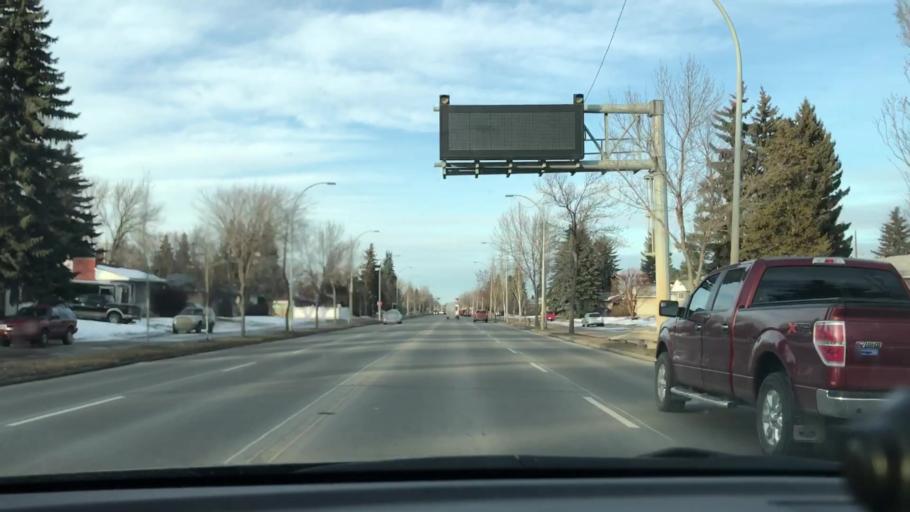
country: CA
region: Alberta
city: Edmonton
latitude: 53.5293
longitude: -113.4429
